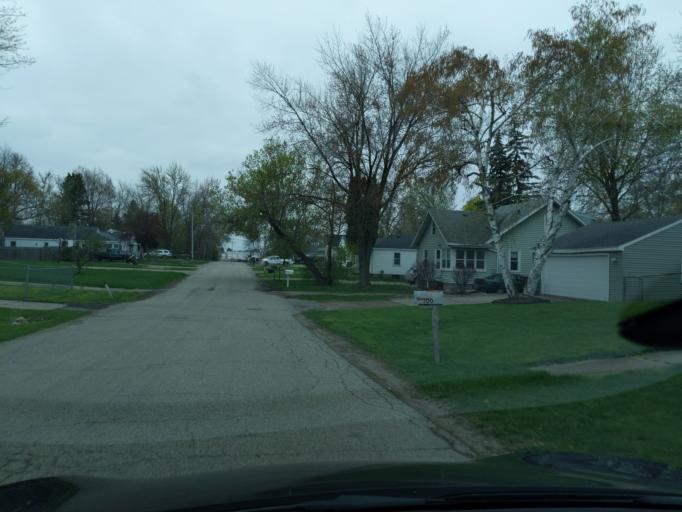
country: US
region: Michigan
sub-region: Ingham County
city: Edgemont Park
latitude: 42.7319
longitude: -84.5844
